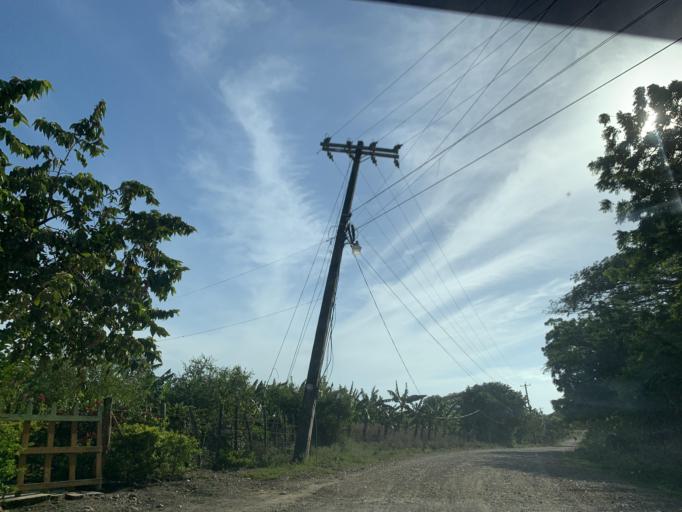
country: DO
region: Puerto Plata
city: Luperon
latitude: 19.8787
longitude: -70.9278
